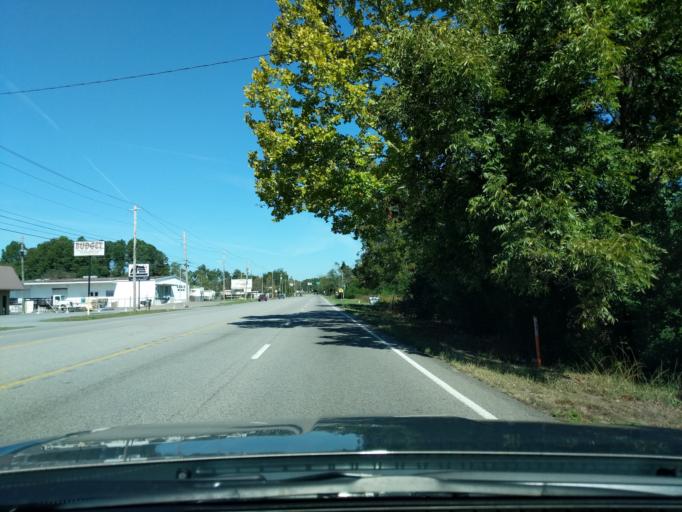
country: US
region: Georgia
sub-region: Richmond County
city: Augusta
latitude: 33.4250
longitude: -82.0061
